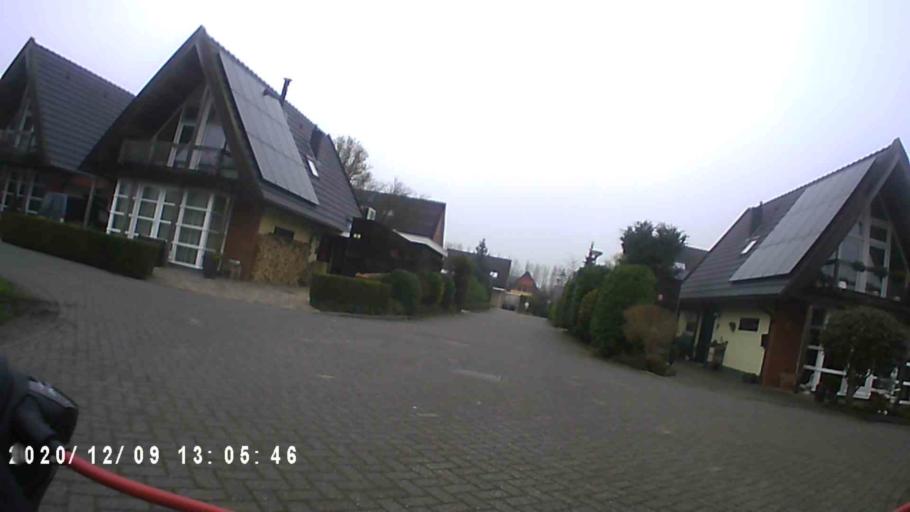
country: NL
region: Groningen
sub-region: Gemeente Groningen
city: Oosterpark
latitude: 53.2425
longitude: 6.6215
